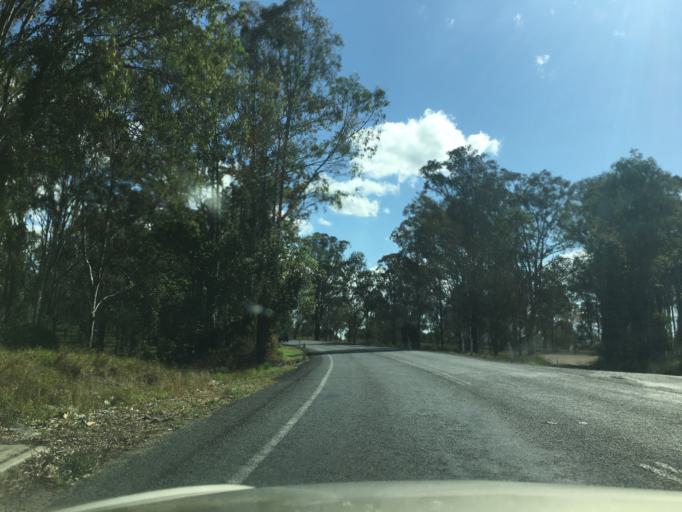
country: AU
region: Queensland
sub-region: Logan
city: Chambers Flat
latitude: -27.7572
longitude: 153.1134
